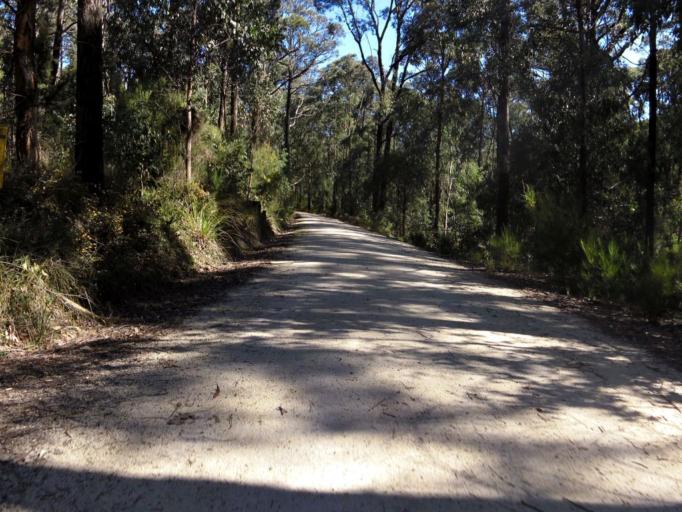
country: AU
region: Victoria
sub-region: Latrobe
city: Moe
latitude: -38.3768
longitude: 146.1960
